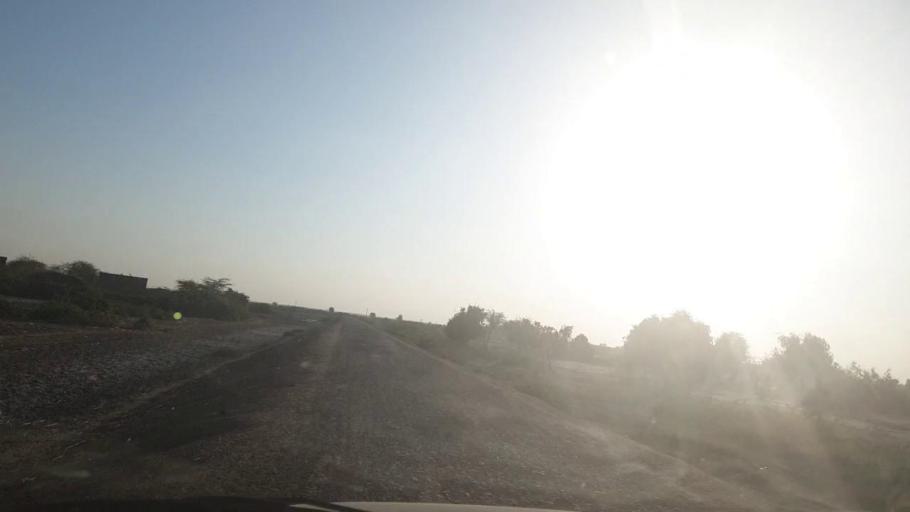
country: PK
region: Sindh
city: Mirpur Khas
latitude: 25.4626
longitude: 69.1055
